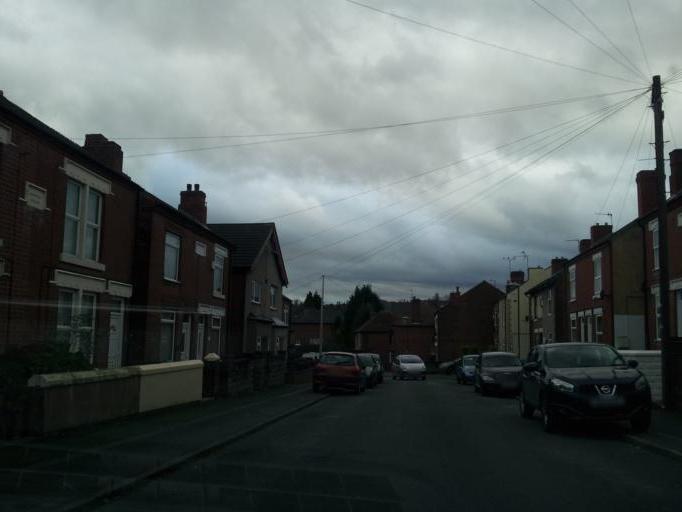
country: GB
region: England
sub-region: Nottinghamshire
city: Eastwood
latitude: 52.9875
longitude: -1.3110
